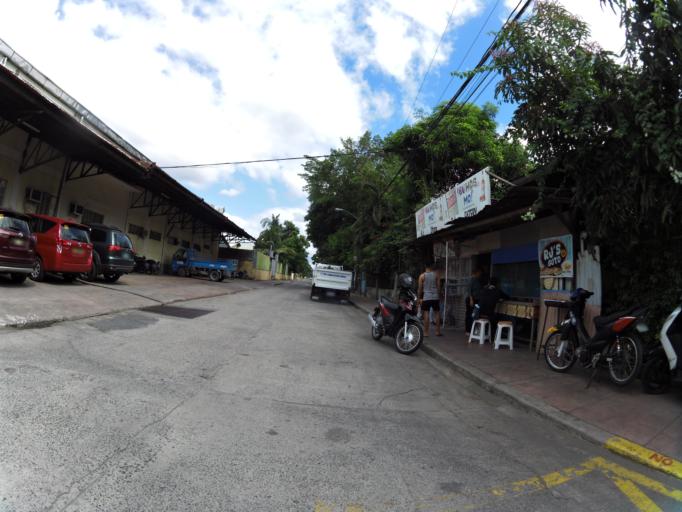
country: PH
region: Calabarzon
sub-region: Province of Rizal
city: Antipolo
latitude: 14.6387
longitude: 121.1117
